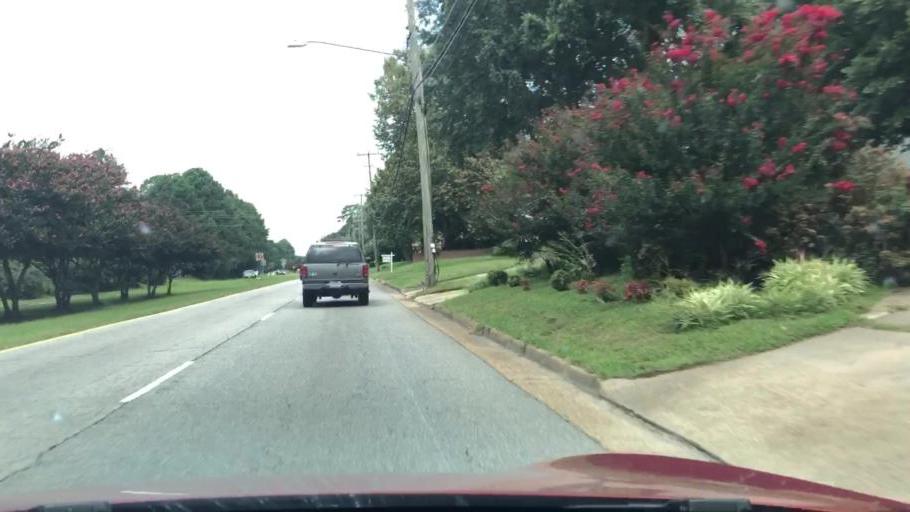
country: US
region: Virginia
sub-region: City of Chesapeake
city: Chesapeake
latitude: 36.8851
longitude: -76.1350
